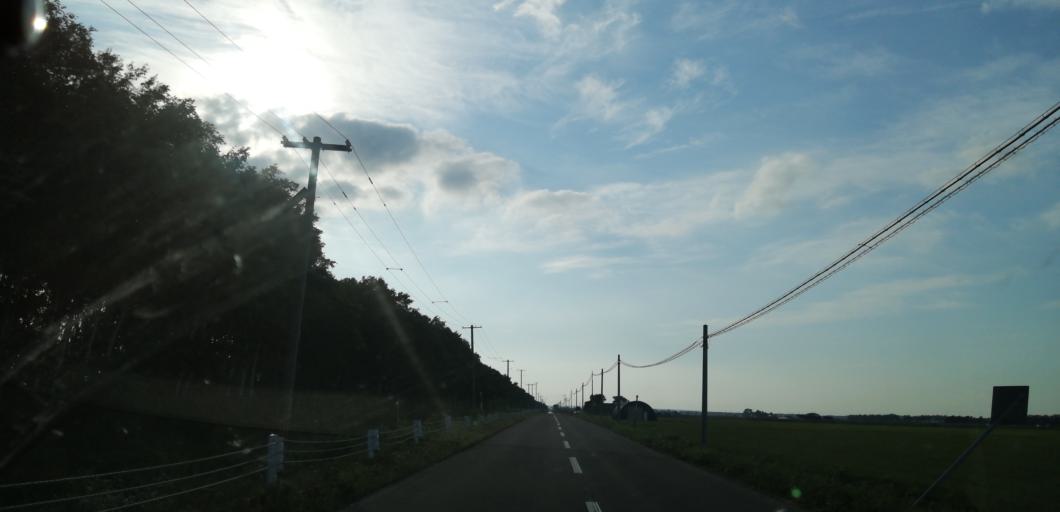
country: JP
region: Hokkaido
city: Chitose
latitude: 42.9376
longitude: 141.7048
